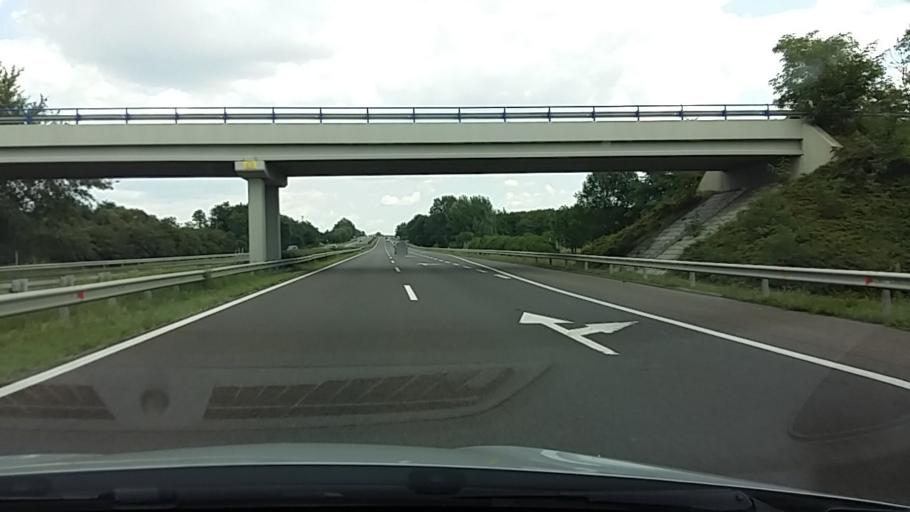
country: HU
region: Heves
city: Kal
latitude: 47.7191
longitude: 20.2707
